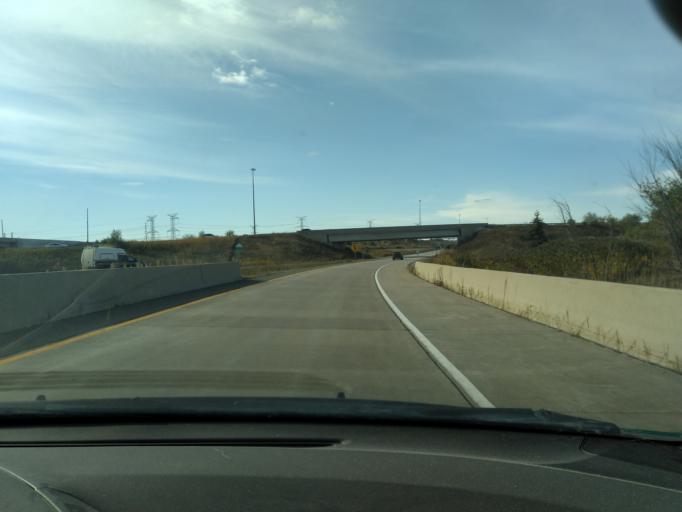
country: CA
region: Ontario
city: Mississauga
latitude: 43.5305
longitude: -79.7279
